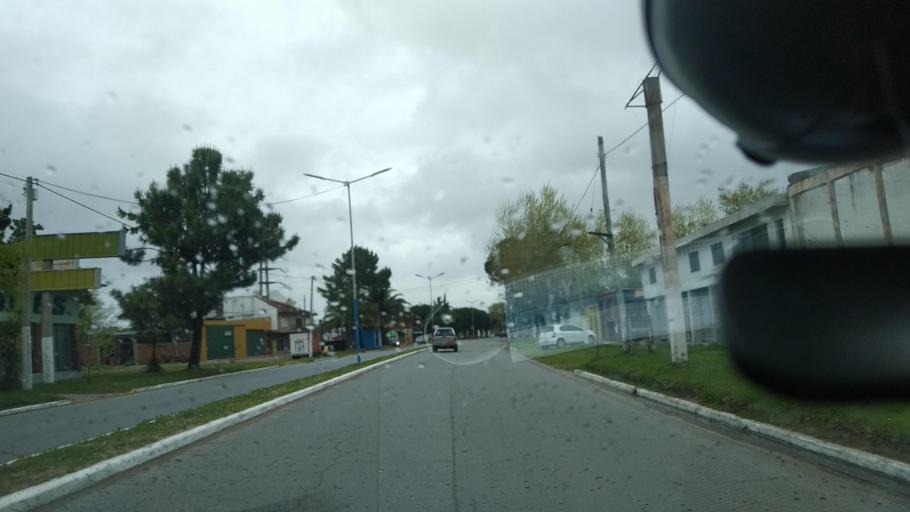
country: AR
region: Buenos Aires
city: San Clemente del Tuyu
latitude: -36.3807
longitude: -56.7216
